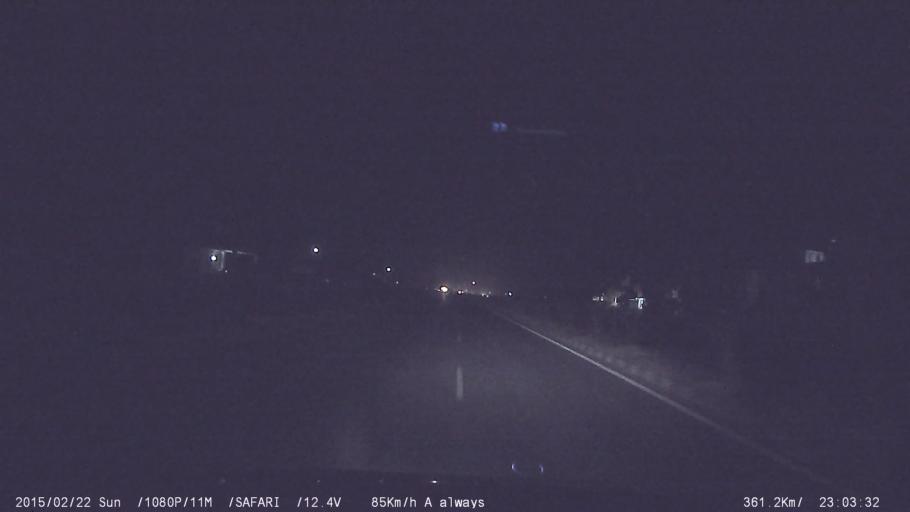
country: IN
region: Tamil Nadu
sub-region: Namakkal
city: Rasipuram
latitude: 11.3901
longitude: 78.1611
